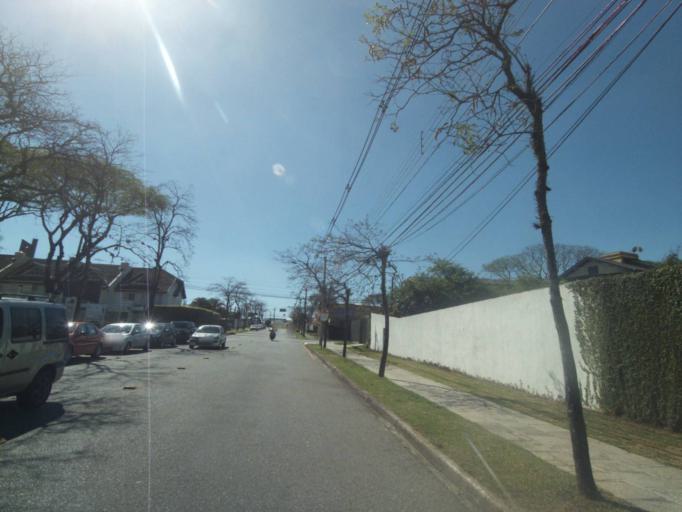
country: BR
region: Parana
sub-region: Curitiba
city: Curitiba
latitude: -25.3957
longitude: -49.2391
